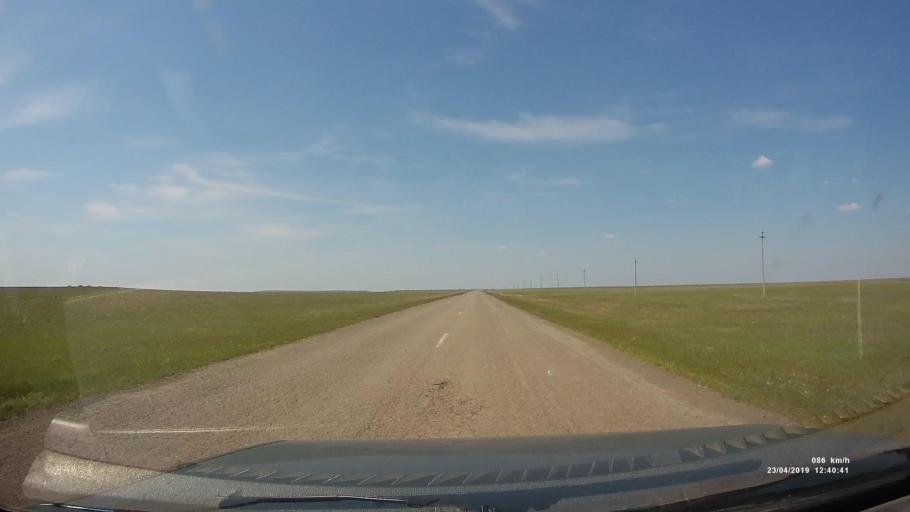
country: RU
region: Kalmykiya
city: Yashalta
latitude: 46.4422
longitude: 42.6928
